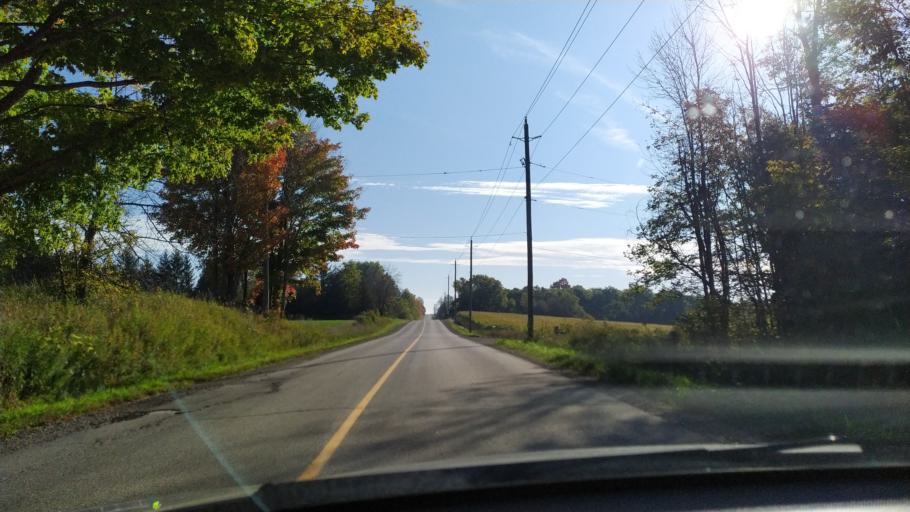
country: CA
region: Ontario
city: Stratford
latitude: 43.4959
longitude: -80.7619
